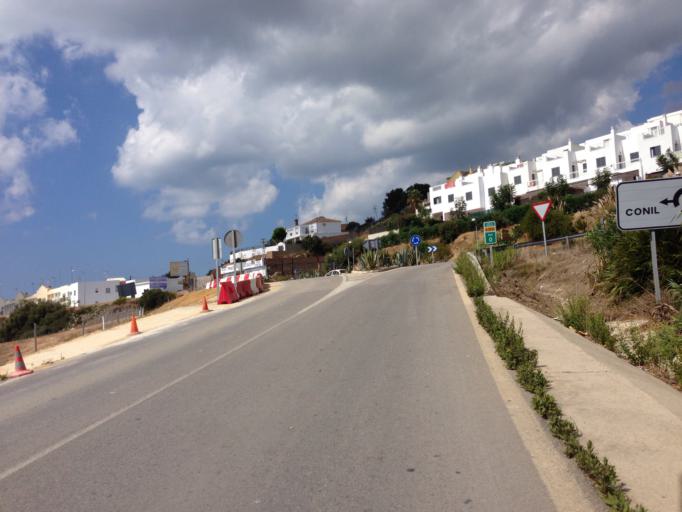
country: ES
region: Andalusia
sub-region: Provincia de Cadiz
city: Conil de la Frontera
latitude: 36.2767
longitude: -6.0793
